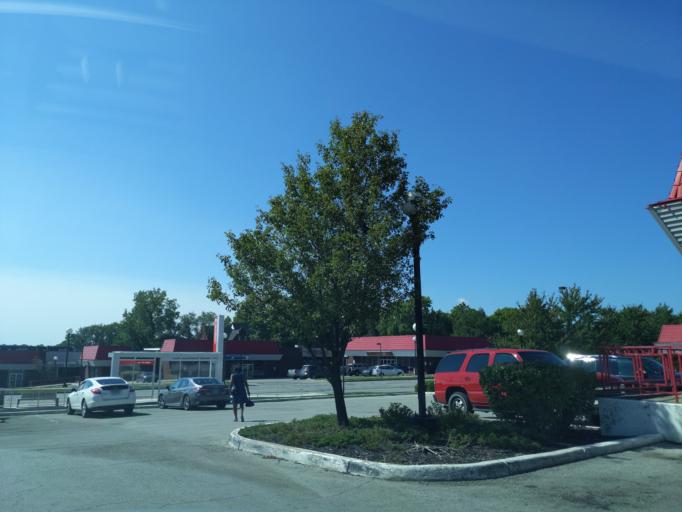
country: US
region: Missouri
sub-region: Jackson County
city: Kansas City
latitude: 39.0995
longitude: -94.5562
